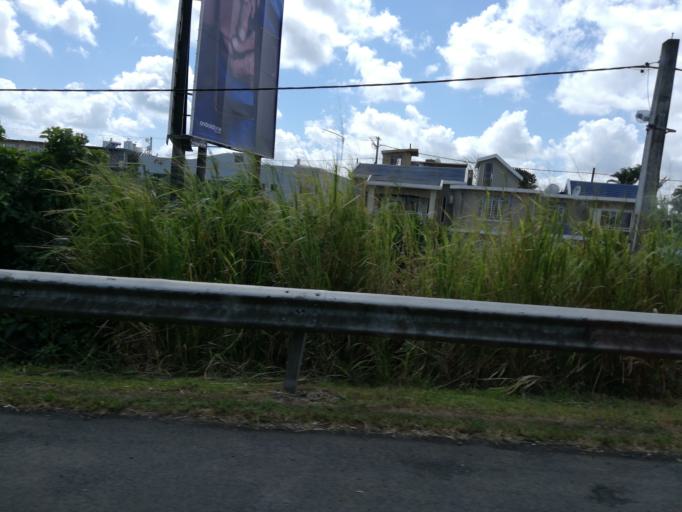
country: MU
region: Plaines Wilhems
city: Quatre Bornes
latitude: -20.2806
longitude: 57.5093
